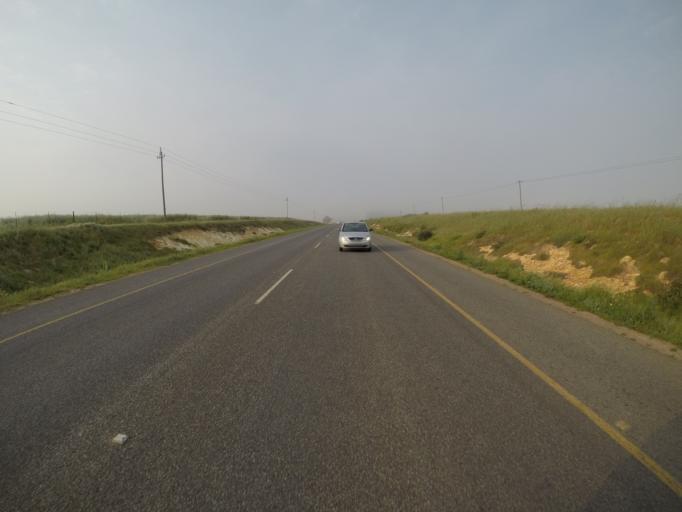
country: ZA
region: Western Cape
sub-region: City of Cape Town
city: Kraaifontein
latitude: -33.6606
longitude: 18.7081
